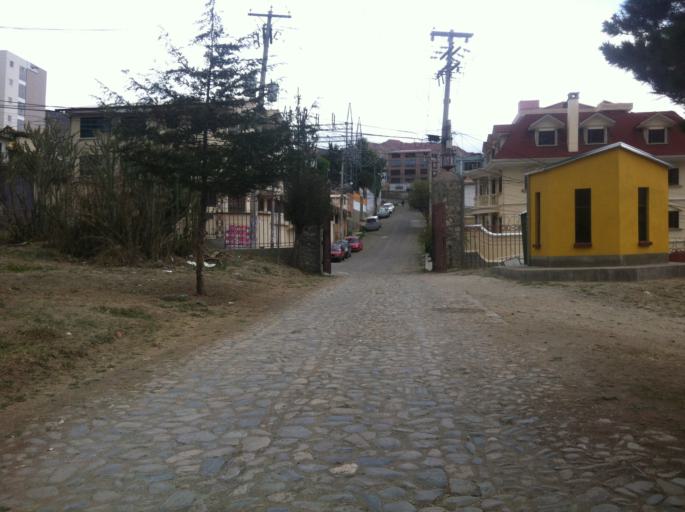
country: BO
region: La Paz
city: La Paz
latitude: -16.5391
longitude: -68.0642
